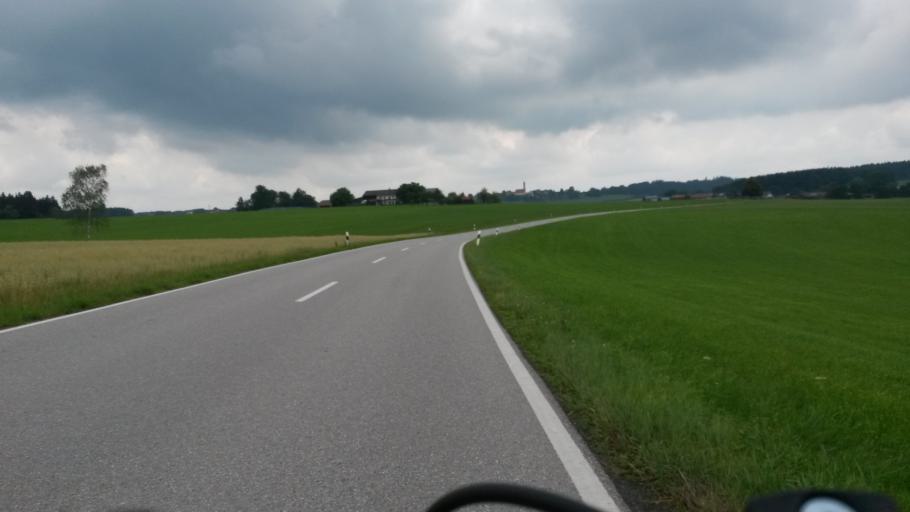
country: DE
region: Bavaria
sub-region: Upper Bavaria
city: Hoslwang
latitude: 47.9366
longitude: 12.3426
